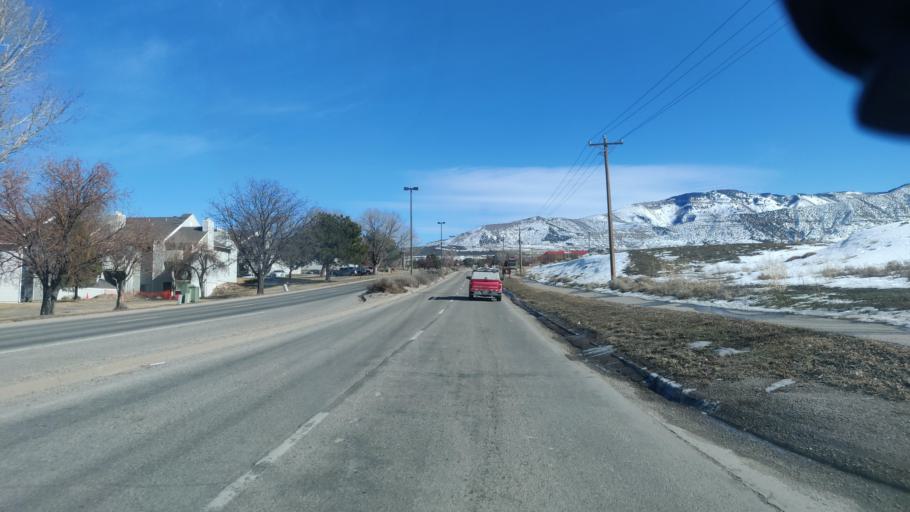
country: US
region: Colorado
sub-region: Garfield County
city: Battlement Mesa
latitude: 39.4413
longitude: -108.0332
